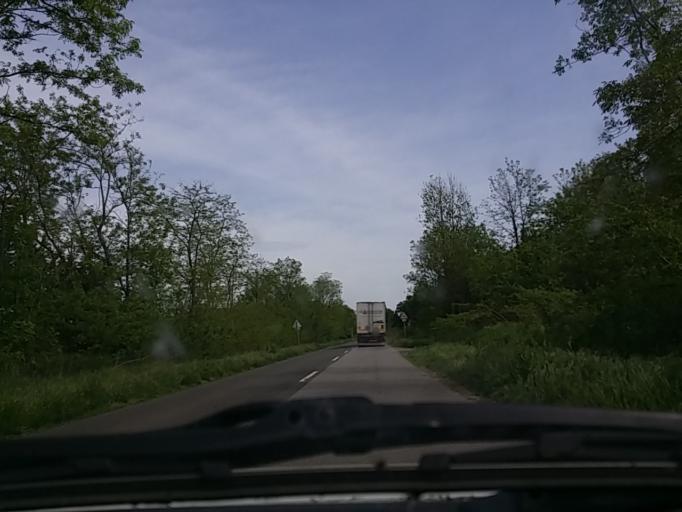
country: HU
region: Baranya
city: Vajszlo
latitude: 45.8681
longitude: 17.9623
